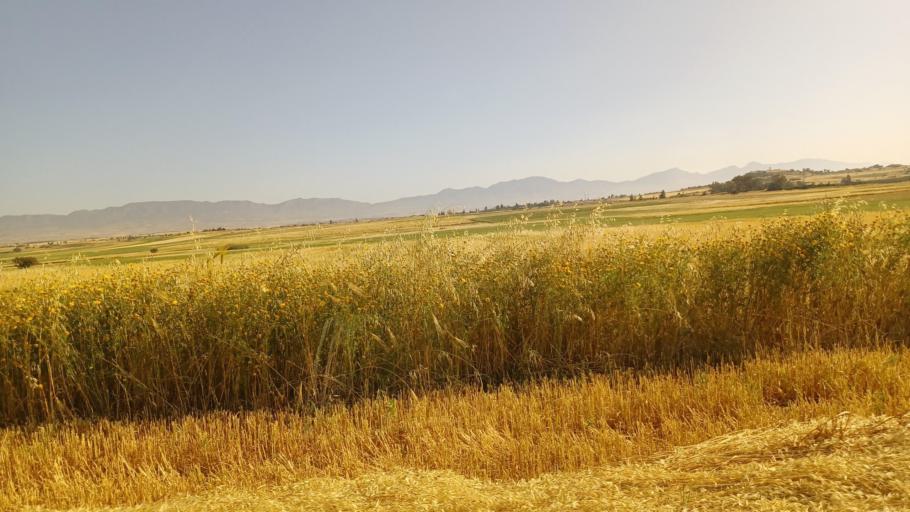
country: CY
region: Lefkosia
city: Mammari
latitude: 35.1634
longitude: 33.2403
